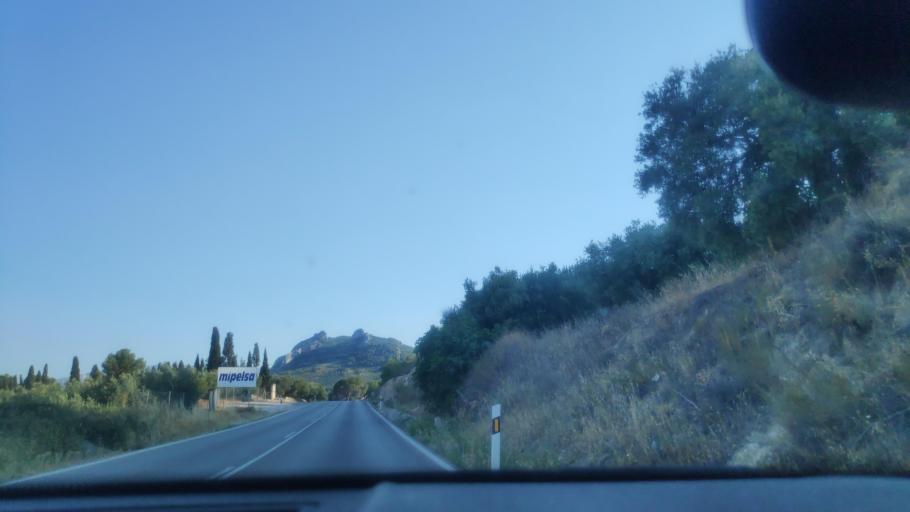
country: ES
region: Andalusia
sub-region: Provincia de Jaen
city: Jaen
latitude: 37.7582
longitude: -3.7902
